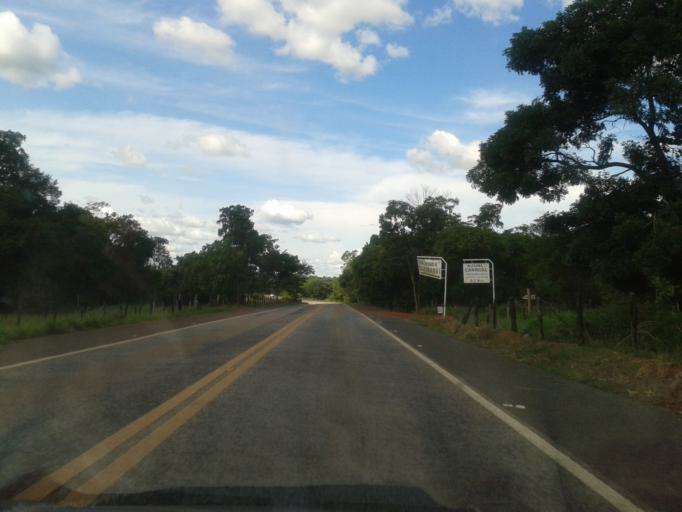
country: BR
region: Goias
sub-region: Mozarlandia
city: Mozarlandia
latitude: -14.9885
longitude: -50.5833
